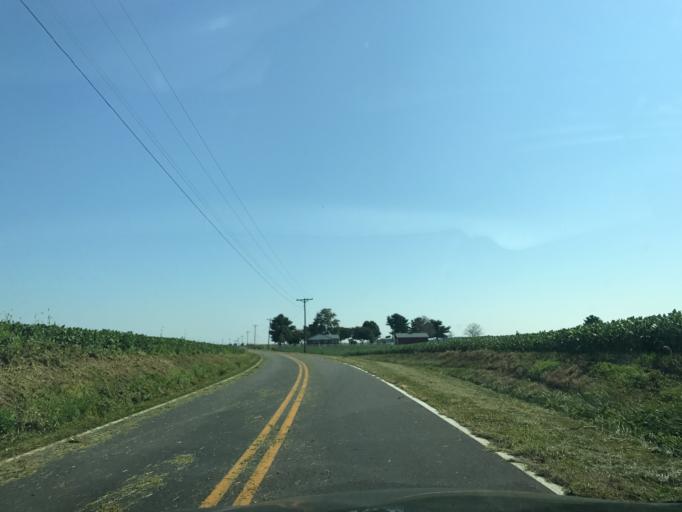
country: US
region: Maryland
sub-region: Queen Anne's County
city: Kingstown
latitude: 39.2695
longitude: -75.9850
